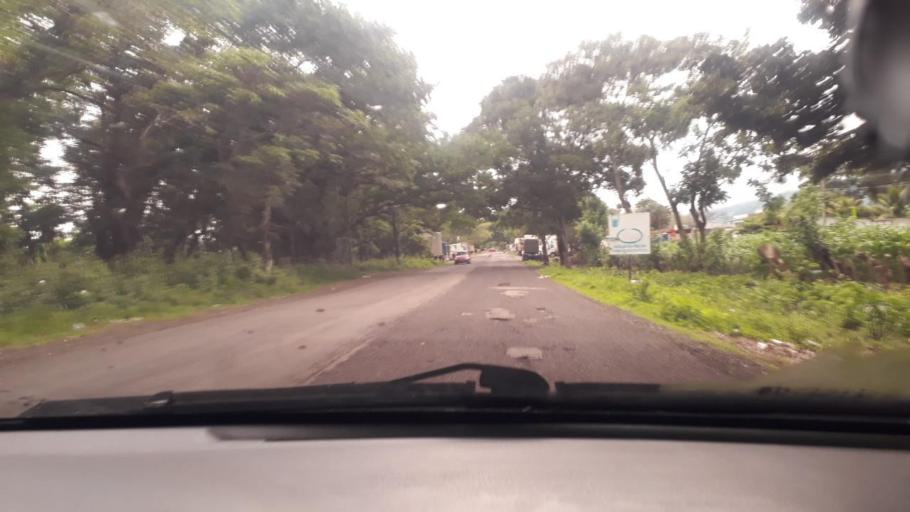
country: GT
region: Jutiapa
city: Jalpatagua
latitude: 14.1301
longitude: -89.9998
